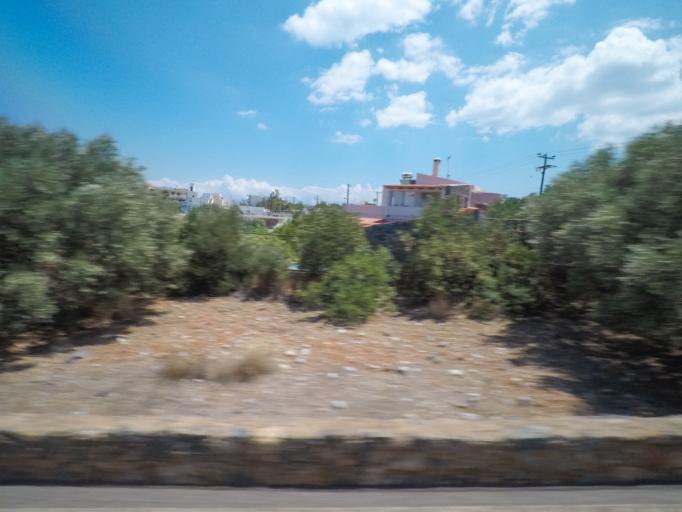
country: GR
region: Crete
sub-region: Nomos Lasithiou
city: Skhisma
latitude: 35.2471
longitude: 25.7272
